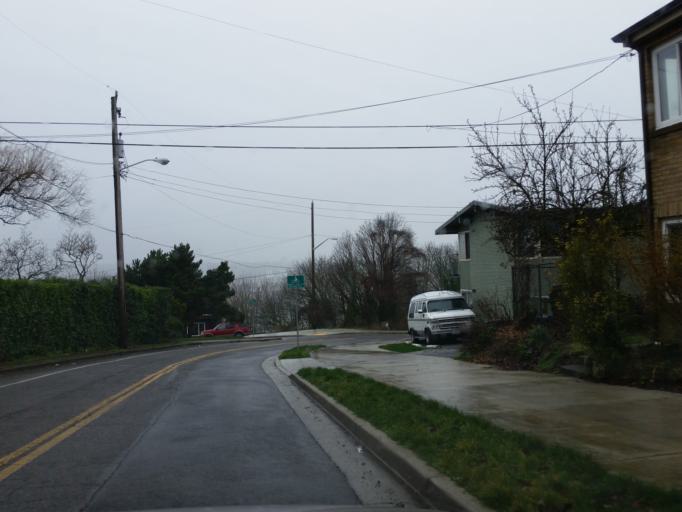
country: US
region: Washington
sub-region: King County
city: Seattle
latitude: 47.5819
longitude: -122.3150
